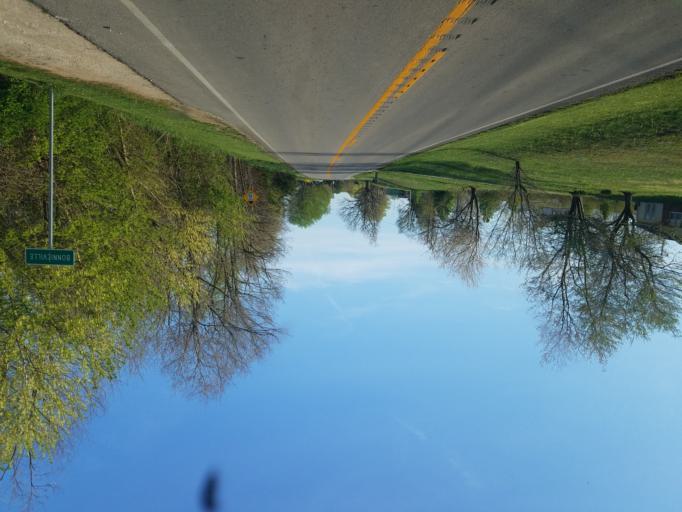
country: US
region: Kentucky
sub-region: Hart County
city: Munfordville
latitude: 37.3919
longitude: -85.9032
